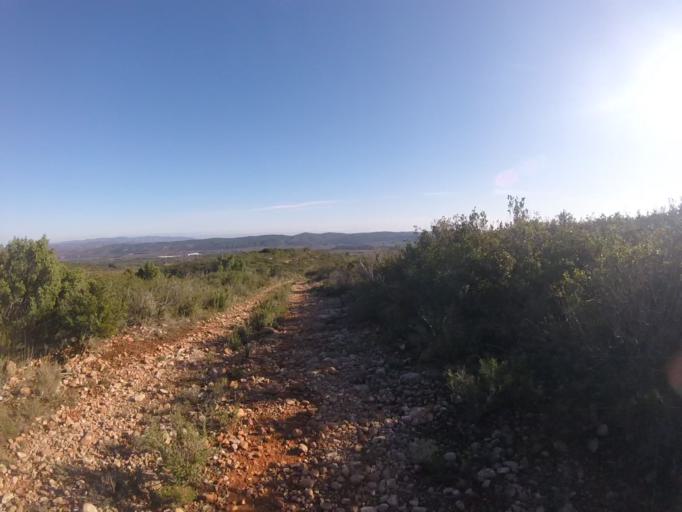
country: ES
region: Valencia
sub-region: Provincia de Castello
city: Sarratella
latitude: 40.2893
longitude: 0.0555
